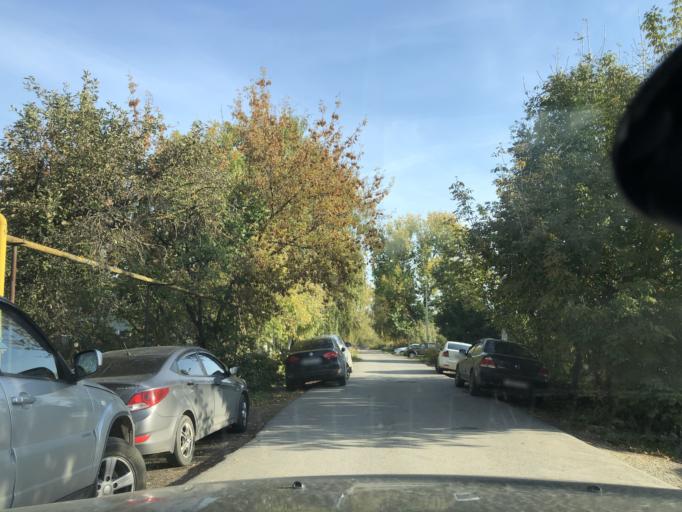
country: RU
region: Tula
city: Tula
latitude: 54.1911
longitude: 37.6298
